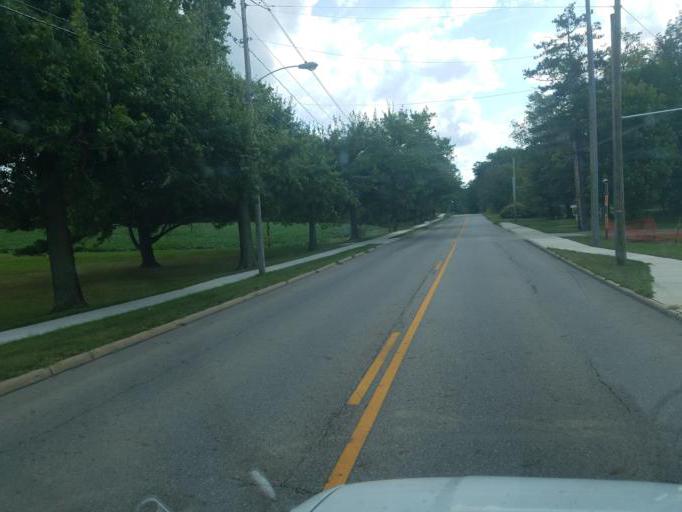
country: US
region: Ohio
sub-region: Portage County
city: Hiram
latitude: 41.3051
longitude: -81.1439
